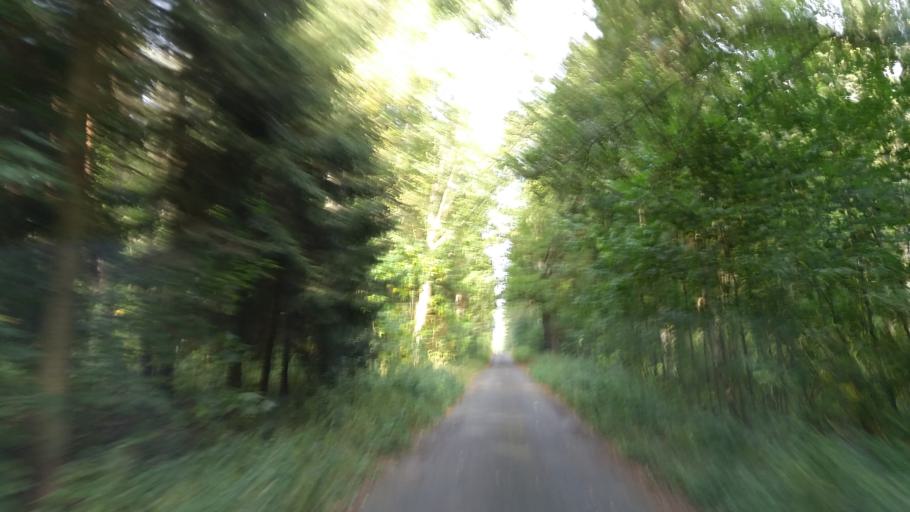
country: PL
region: West Pomeranian Voivodeship
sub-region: Powiat choszczenski
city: Krzecin
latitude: 52.9893
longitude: 15.4665
